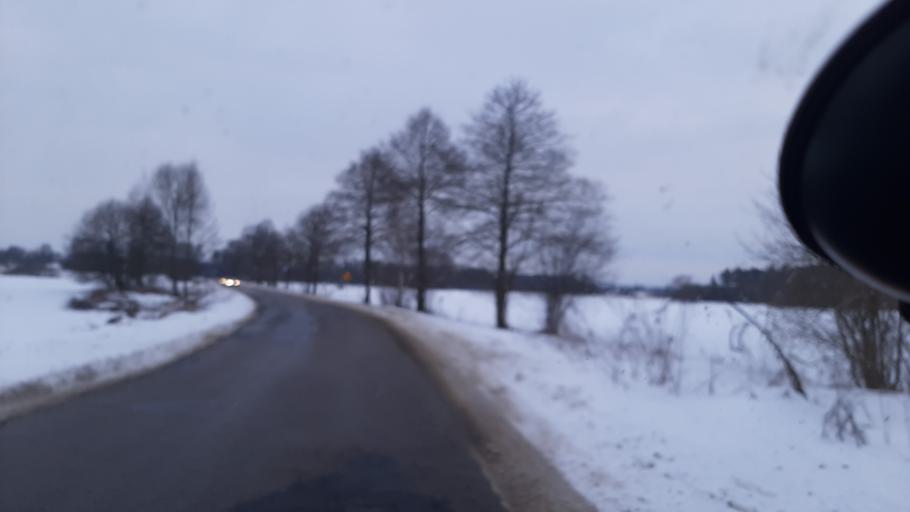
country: PL
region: Lublin Voivodeship
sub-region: Powiat pulawski
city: Kurow
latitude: 51.4156
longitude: 22.2012
